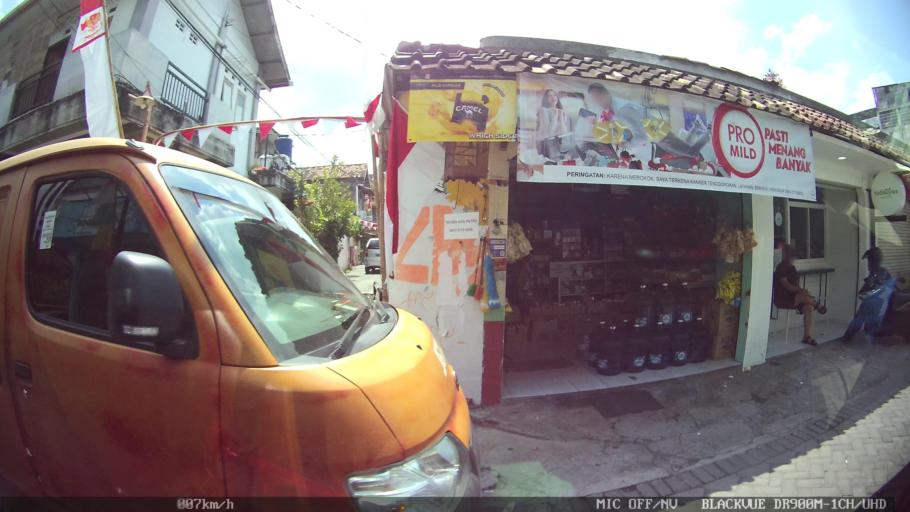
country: ID
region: Daerah Istimewa Yogyakarta
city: Yogyakarta
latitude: -7.7732
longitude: 110.3887
